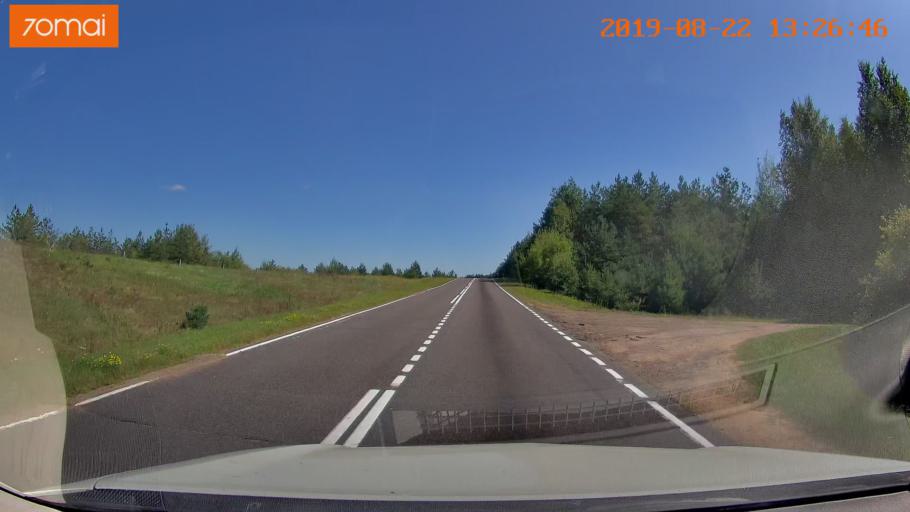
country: BY
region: Minsk
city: Staryya Darohi
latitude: 53.2081
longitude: 28.0697
